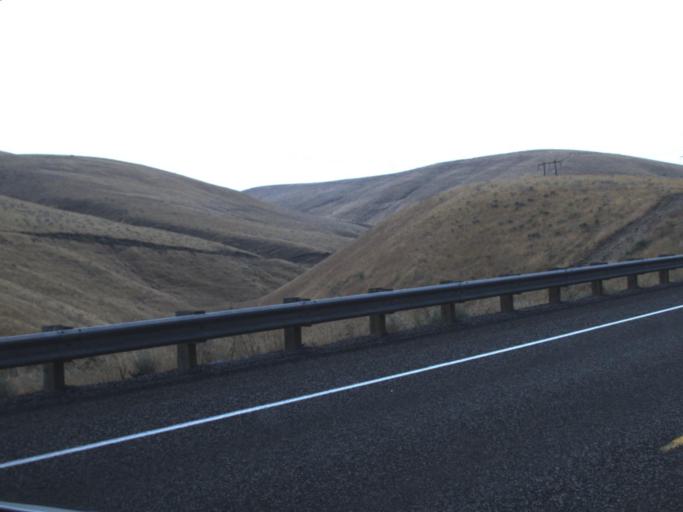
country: US
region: Washington
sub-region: Yakima County
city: Sunnyside
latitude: 46.4822
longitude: -119.9203
